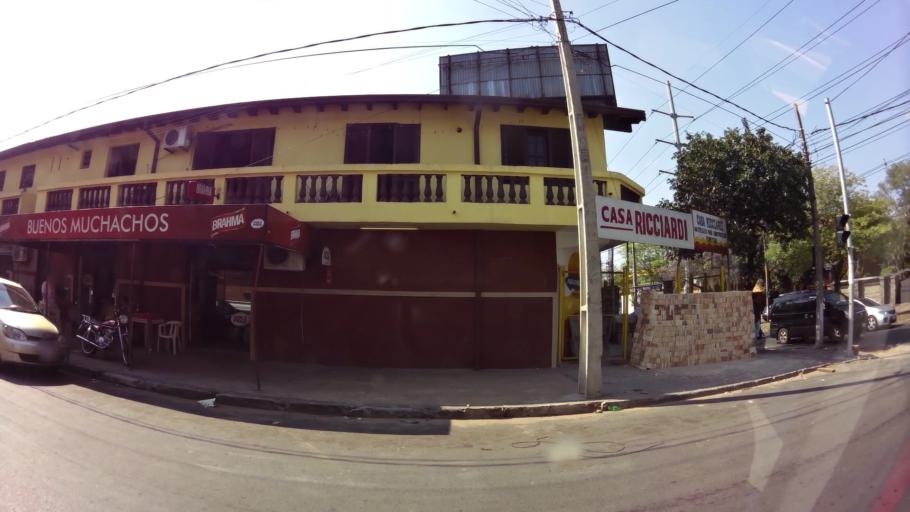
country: PY
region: Asuncion
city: Asuncion
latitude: -25.3156
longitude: -57.6303
